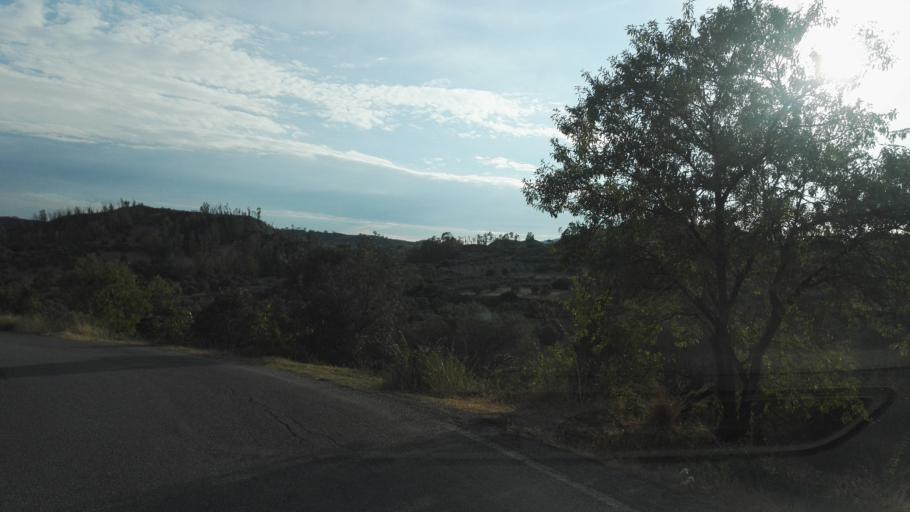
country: IT
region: Calabria
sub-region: Provincia di Reggio Calabria
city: Stignano
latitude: 38.3978
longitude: 16.4700
